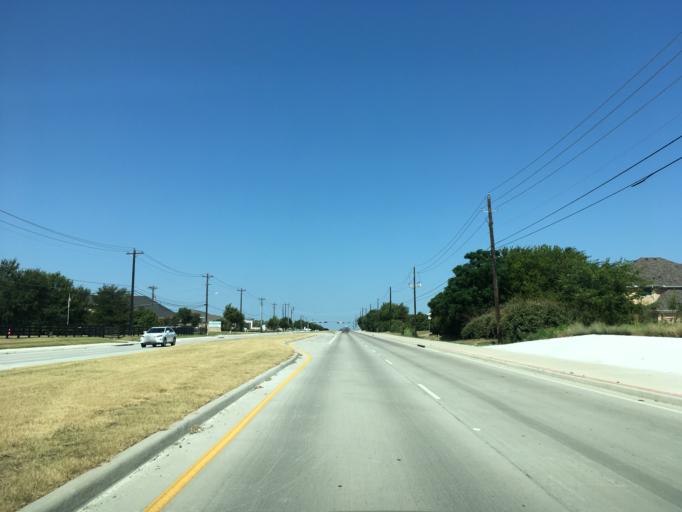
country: US
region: Texas
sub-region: Collin County
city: Fairview
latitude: 33.1296
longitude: -96.6240
